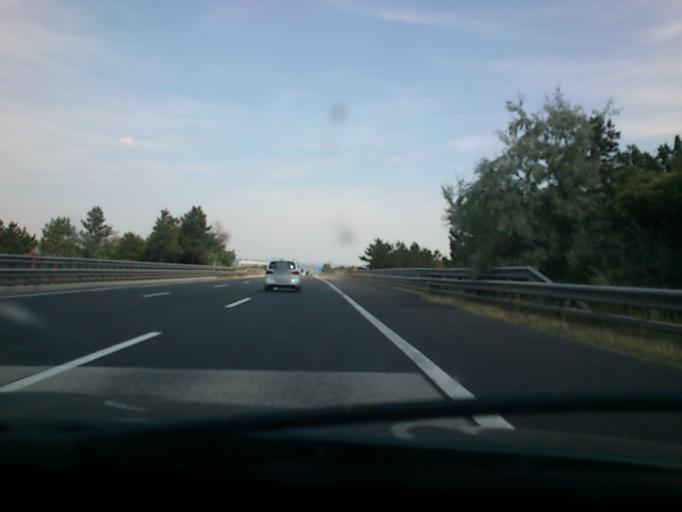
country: AT
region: Lower Austria
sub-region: Wiener Neustadt Stadt
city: Wiener Neustadt
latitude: 47.7866
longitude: 16.2054
